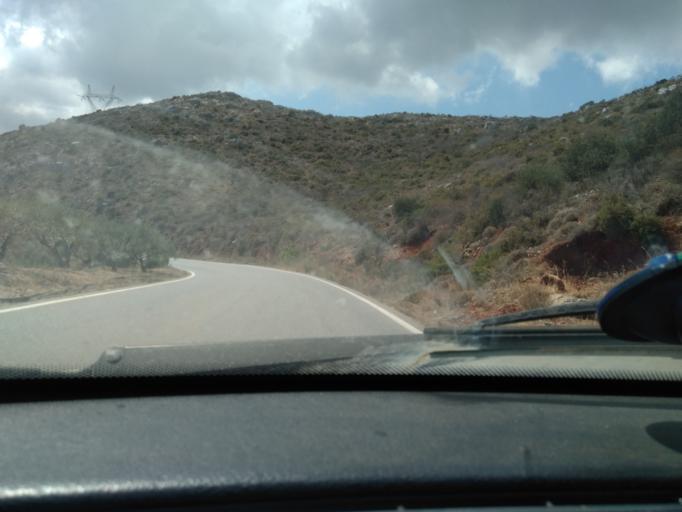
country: GR
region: Crete
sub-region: Nomos Lasithiou
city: Siteia
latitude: 35.1136
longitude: 26.0565
